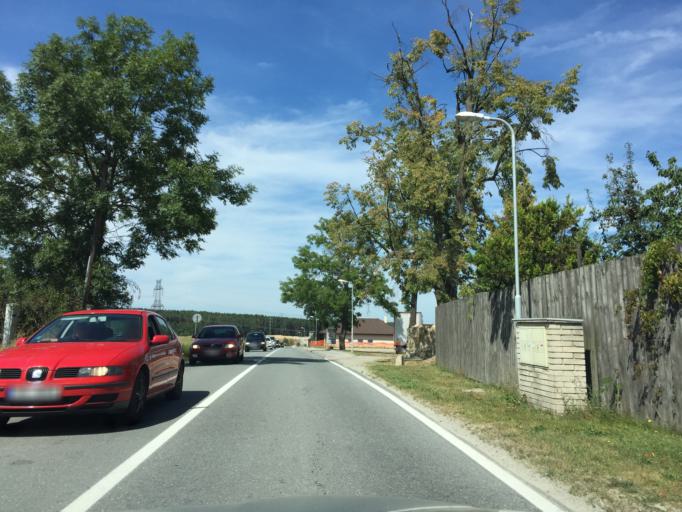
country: CZ
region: Jihocesky
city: Sevetin
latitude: 49.1025
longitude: 14.5728
